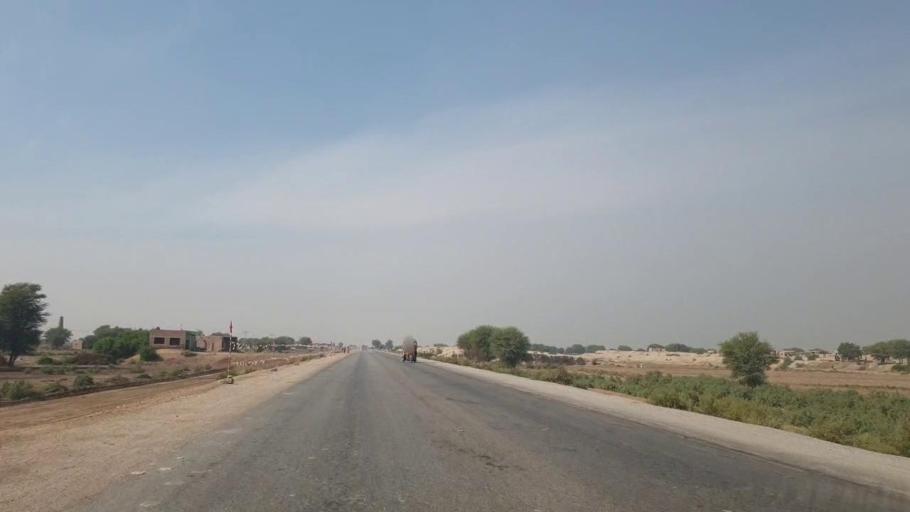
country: PK
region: Sindh
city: Sann
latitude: 25.9865
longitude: 68.1810
